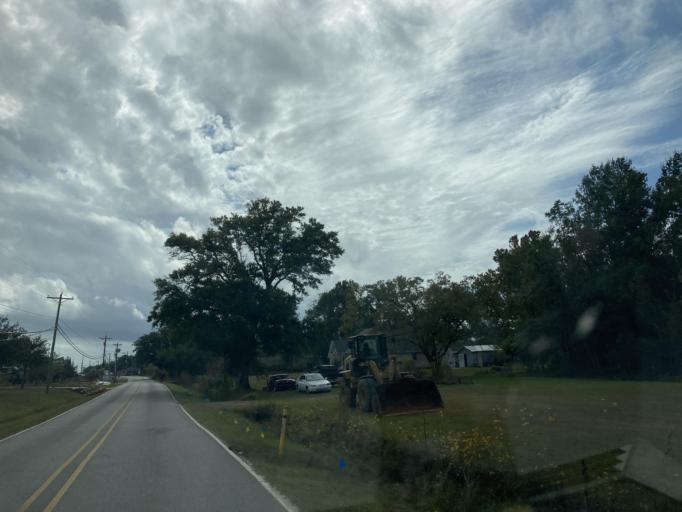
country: US
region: Mississippi
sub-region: Jackson County
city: Gulf Hills
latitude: 30.4389
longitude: -88.8305
